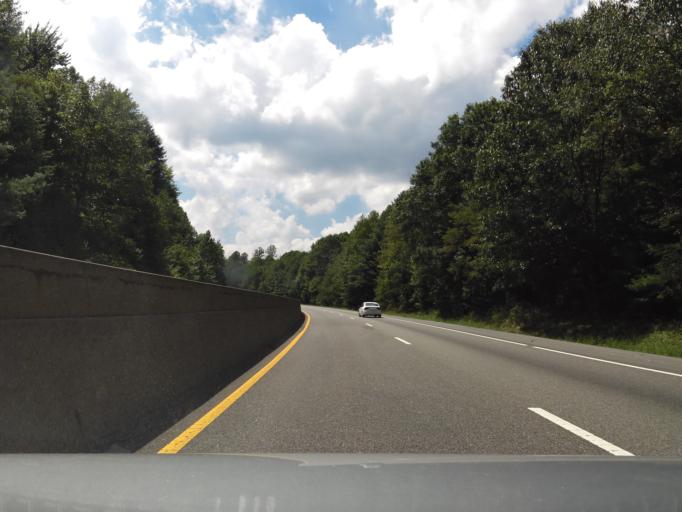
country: US
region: North Carolina
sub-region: Haywood County
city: Cove Creek
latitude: 35.6172
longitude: -83.0115
